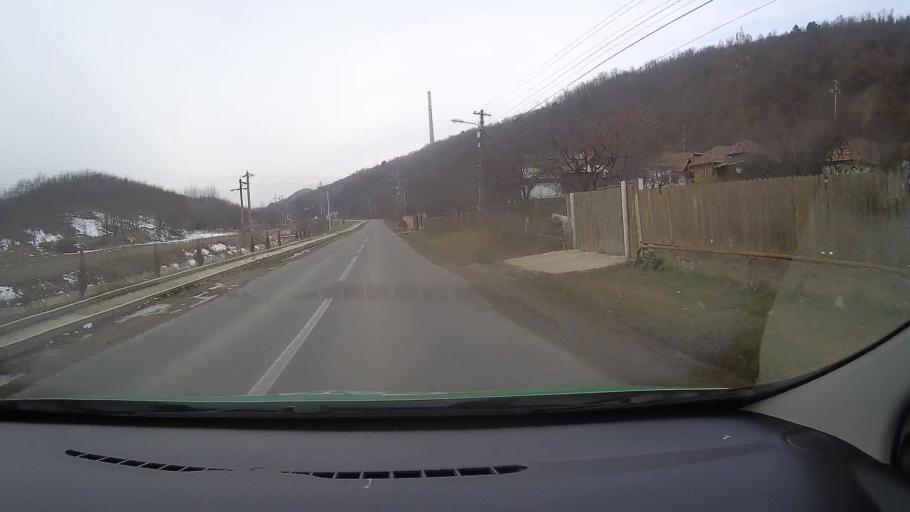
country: RO
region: Alba
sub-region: Oras Zlatna
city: Zlatna
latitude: 46.1028
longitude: 23.2470
